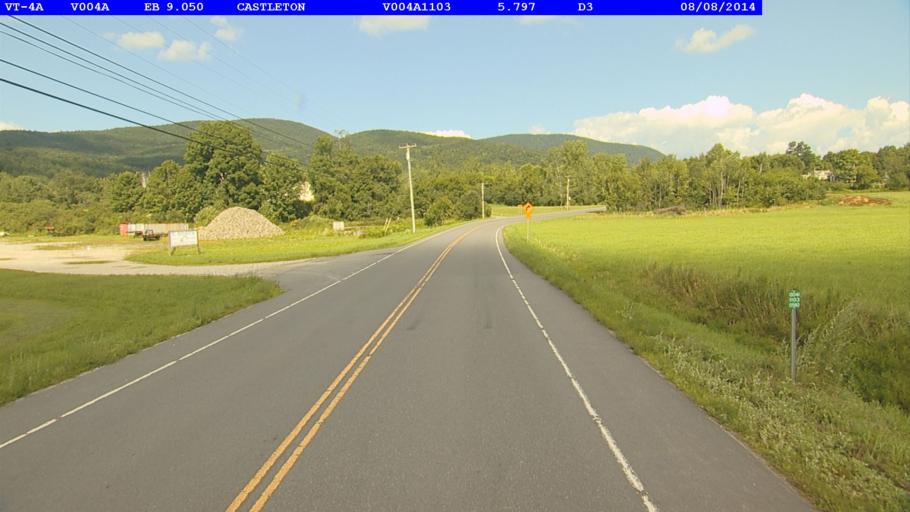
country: US
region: Vermont
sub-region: Rutland County
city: Castleton
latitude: 43.6140
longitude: -73.1326
